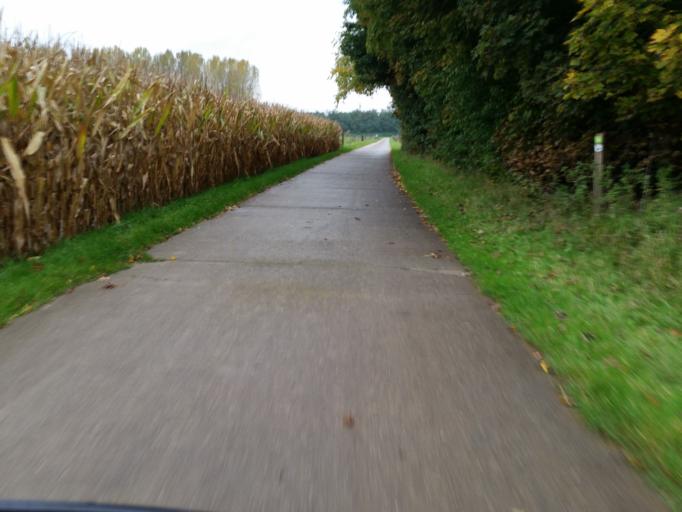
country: BE
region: Flanders
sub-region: Provincie Vlaams-Brabant
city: Zemst
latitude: 50.9807
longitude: 4.4912
